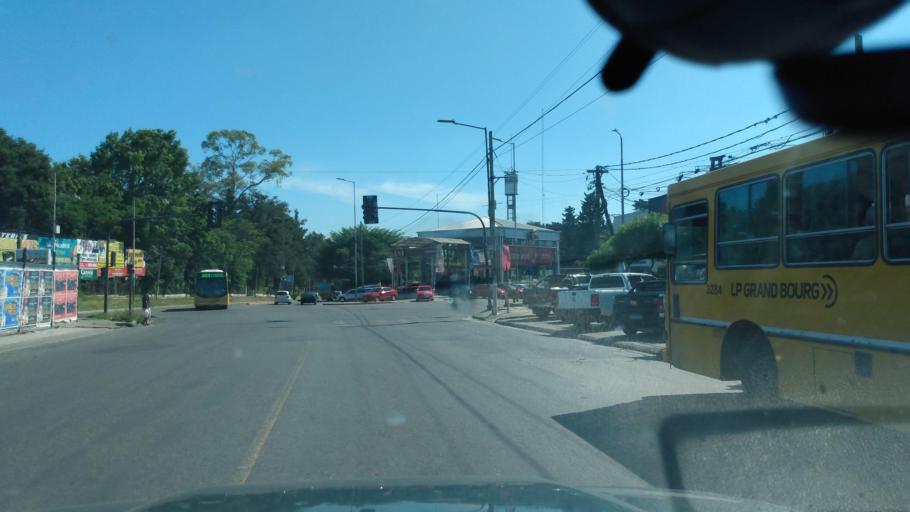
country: AR
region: Buenos Aires
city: Hurlingham
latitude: -34.5510
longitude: -58.7214
